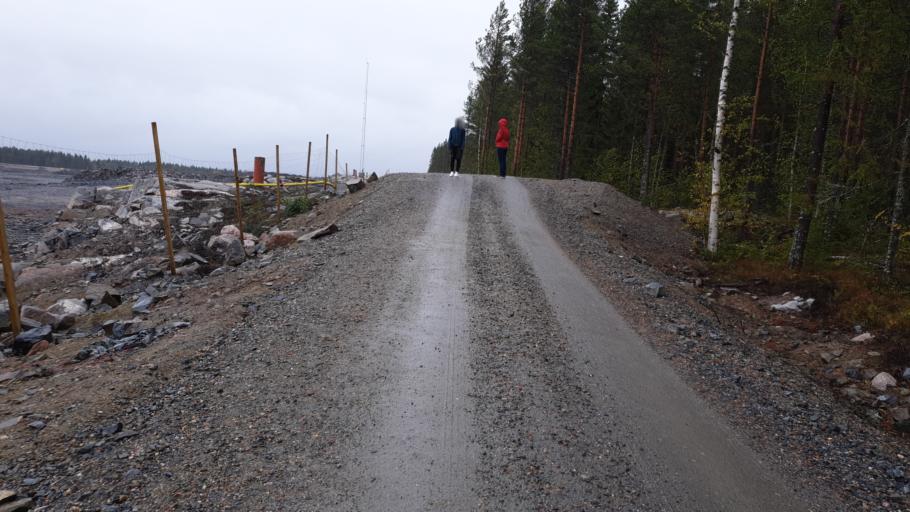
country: SE
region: Vaesterbotten
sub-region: Skelleftea Kommun
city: Soedra Bergsbyn
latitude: 64.7394
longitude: 21.0747
